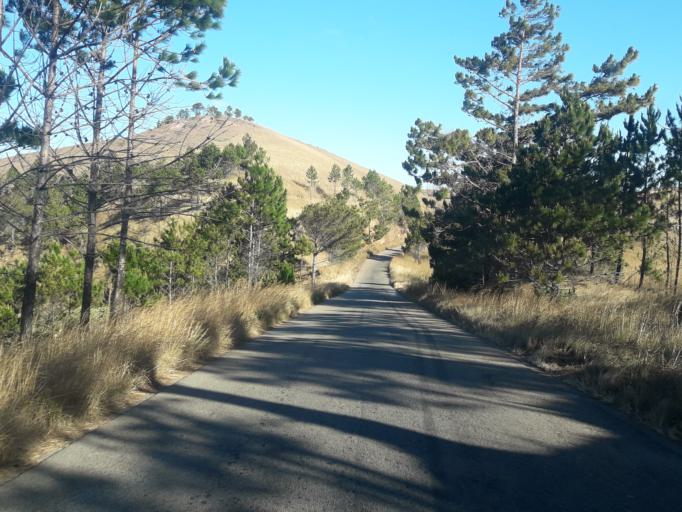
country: MG
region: Analamanga
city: Ankazobe
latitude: -17.9054
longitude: 47.0935
